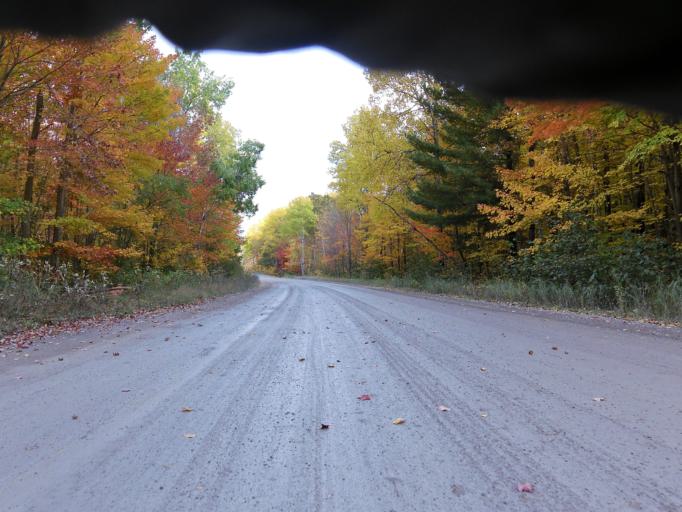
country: CA
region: Ontario
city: Petawawa
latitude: 45.8093
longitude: -77.3570
